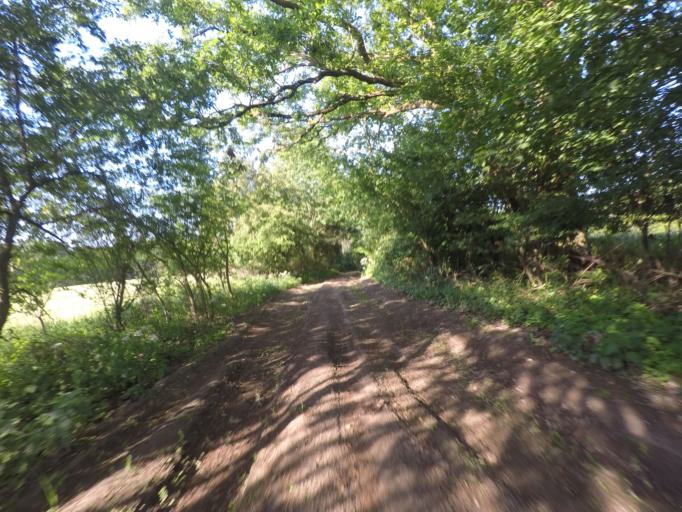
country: DE
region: Brandenburg
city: Melchow
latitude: 52.8735
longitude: 13.6930
